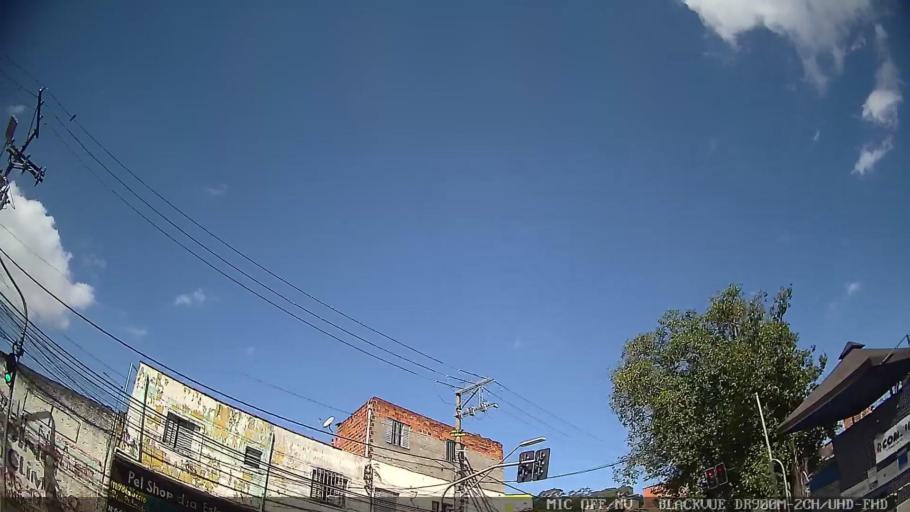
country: BR
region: Sao Paulo
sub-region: Sao Caetano Do Sul
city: Sao Caetano do Sul
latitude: -23.6074
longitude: -46.5981
